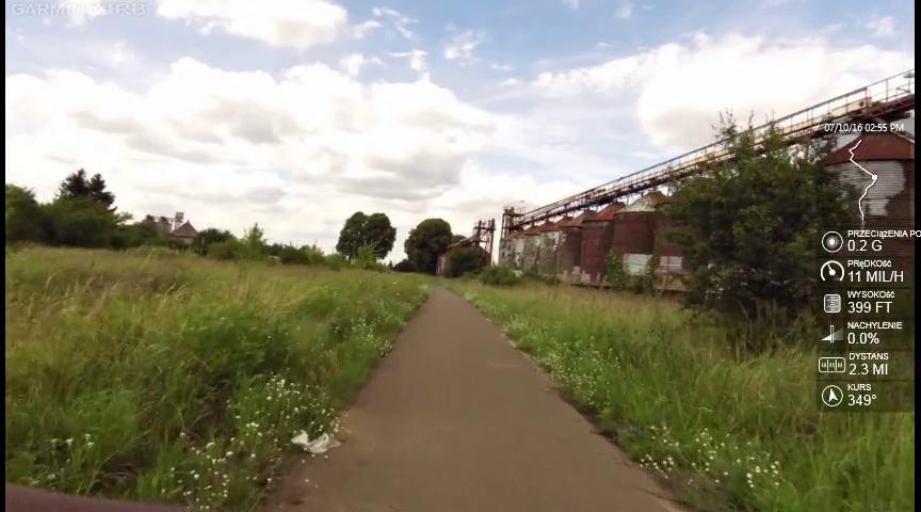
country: PL
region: West Pomeranian Voivodeship
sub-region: Powiat gryfinski
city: Banie
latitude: 53.1006
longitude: 14.6492
